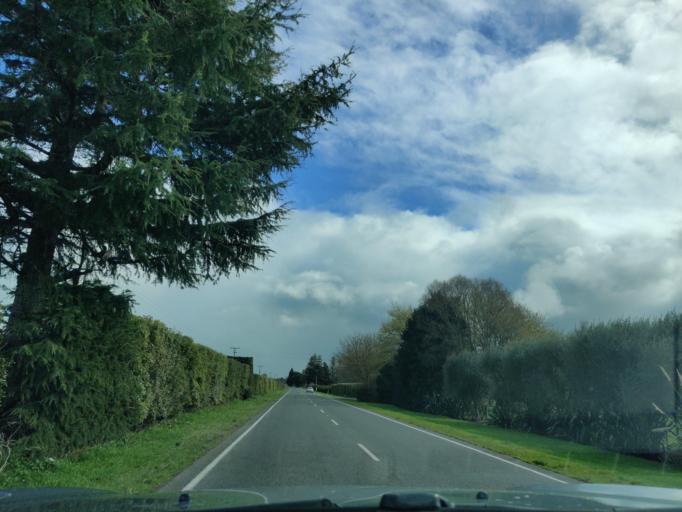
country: NZ
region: Hawke's Bay
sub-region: Hastings District
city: Hastings
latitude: -39.6782
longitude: 176.8541
